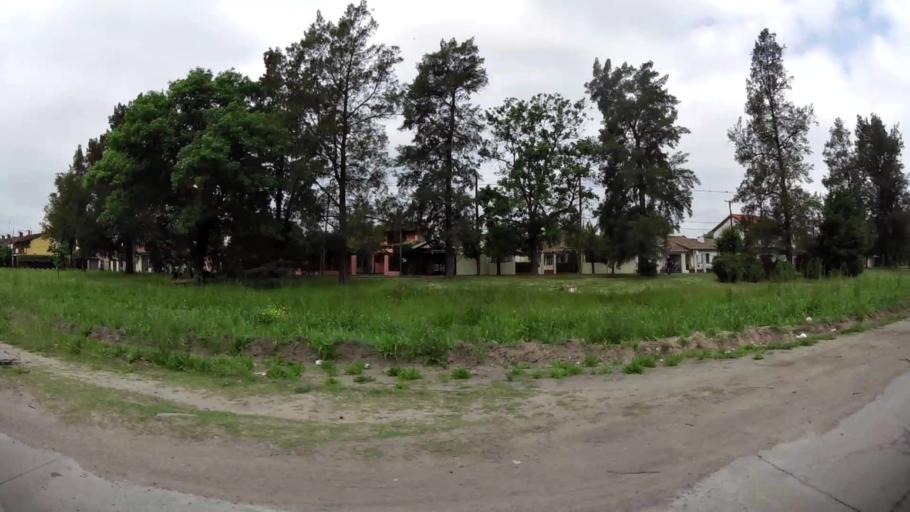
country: AR
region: Buenos Aires
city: San Justo
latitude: -34.7214
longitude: -58.5355
